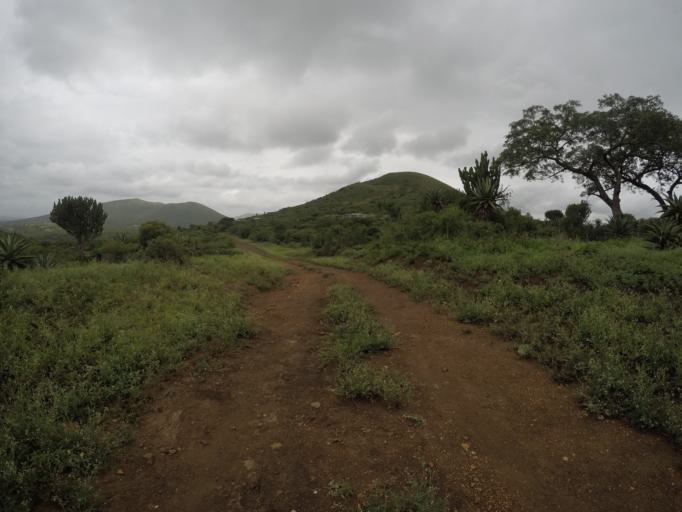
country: ZA
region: KwaZulu-Natal
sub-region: uThungulu District Municipality
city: Empangeni
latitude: -28.5988
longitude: 31.8502
